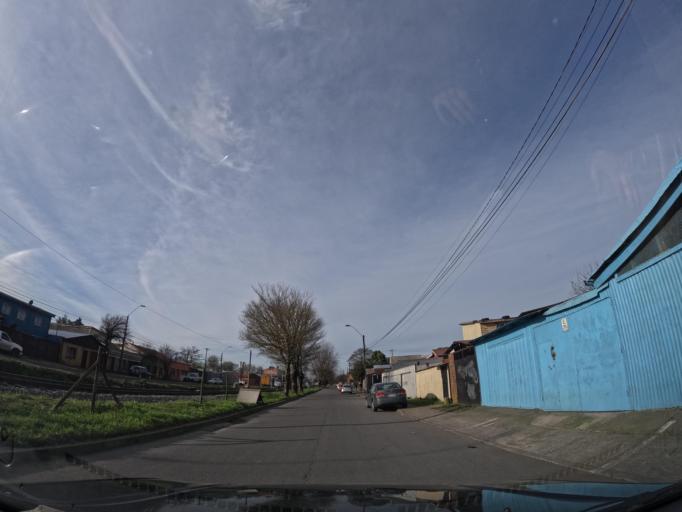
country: CL
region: Biobio
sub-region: Provincia de Concepcion
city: Concepcion
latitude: -36.8154
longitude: -73.0554
